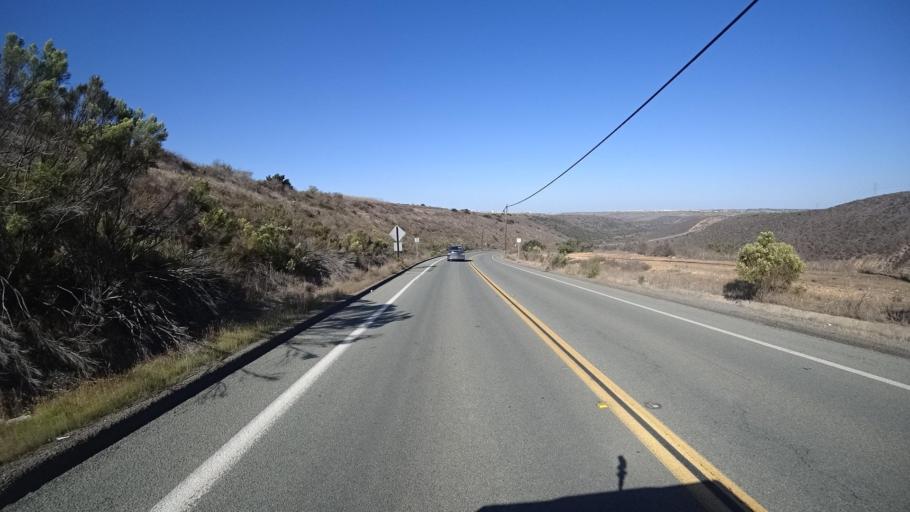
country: MX
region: Baja California
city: Tijuana
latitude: 32.5833
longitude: -116.9215
